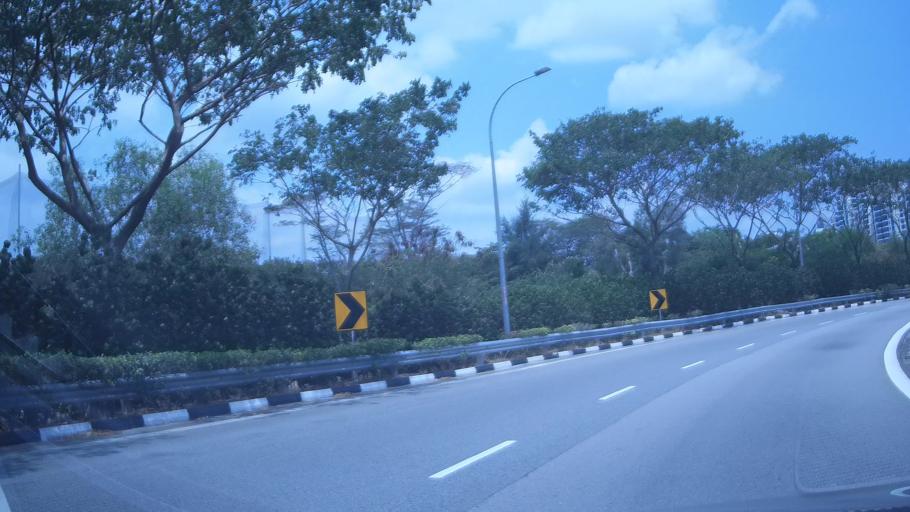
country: SG
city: Singapore
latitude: 1.2939
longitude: 103.8746
